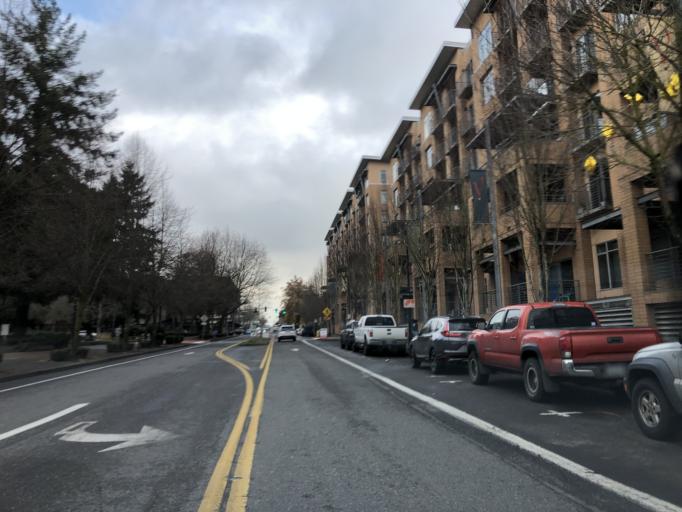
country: US
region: Washington
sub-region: Clark County
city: Vancouver
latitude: 45.6259
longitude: -122.6738
